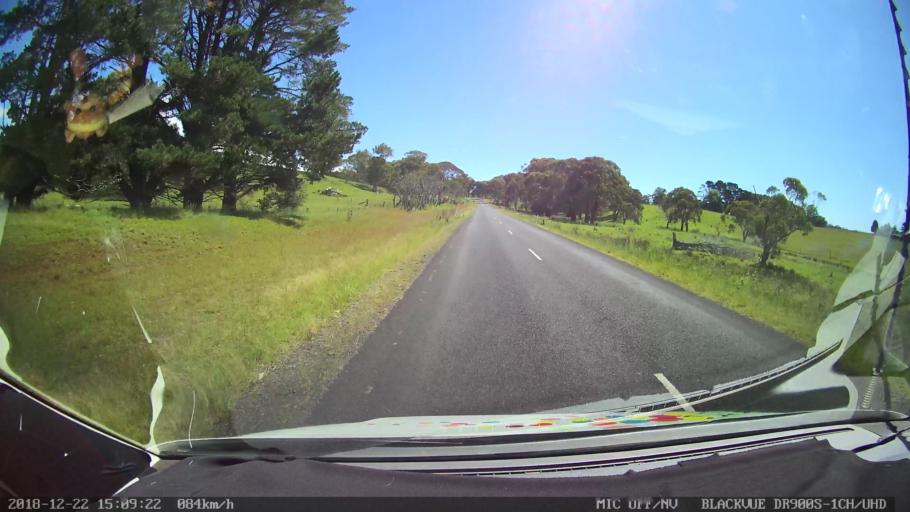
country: AU
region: New South Wales
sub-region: Bellingen
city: Dorrigo
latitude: -30.3234
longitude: 152.4097
